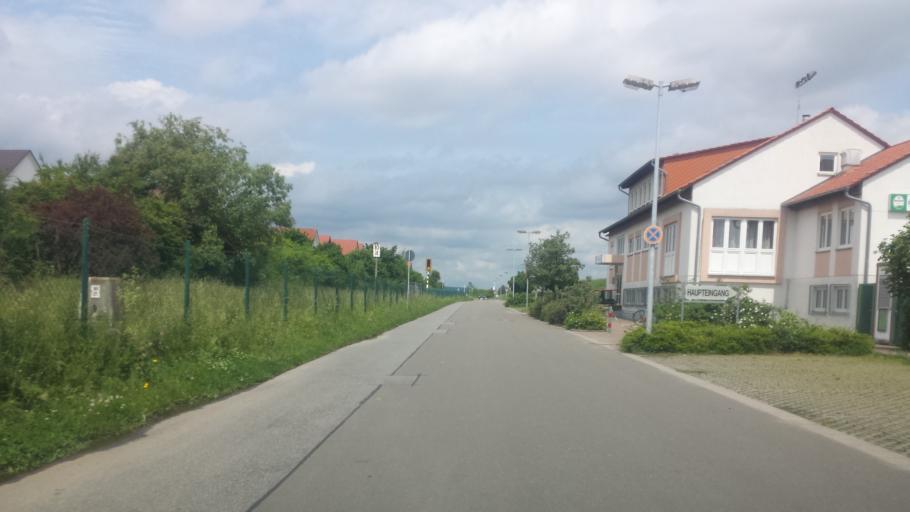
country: DE
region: Rheinland-Pfalz
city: Wachenheim
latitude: 49.4404
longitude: 8.1909
